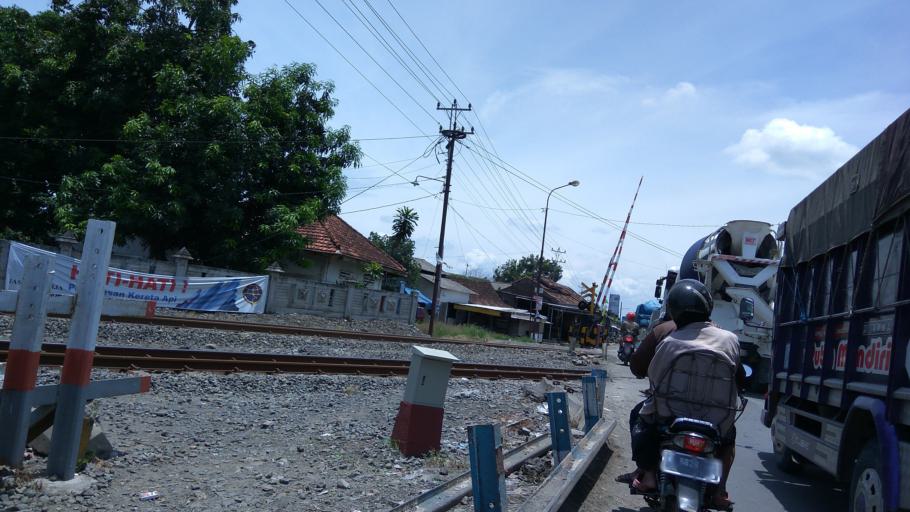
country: ID
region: Central Java
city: Mranggen
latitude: -7.0272
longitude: 110.5239
